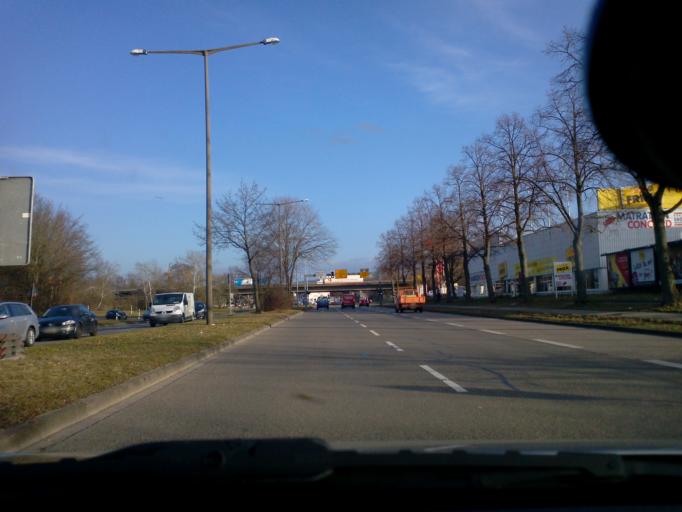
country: DE
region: Baden-Wuerttemberg
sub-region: Karlsruhe Region
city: Karlsruhe
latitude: 48.9904
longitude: 8.3728
